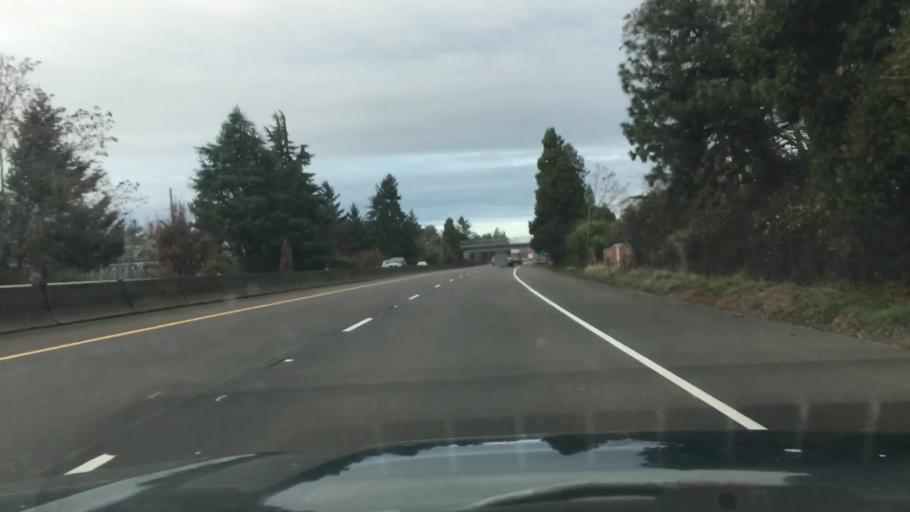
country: US
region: Oregon
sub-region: Lane County
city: Eugene
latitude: 44.0883
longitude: -123.0837
